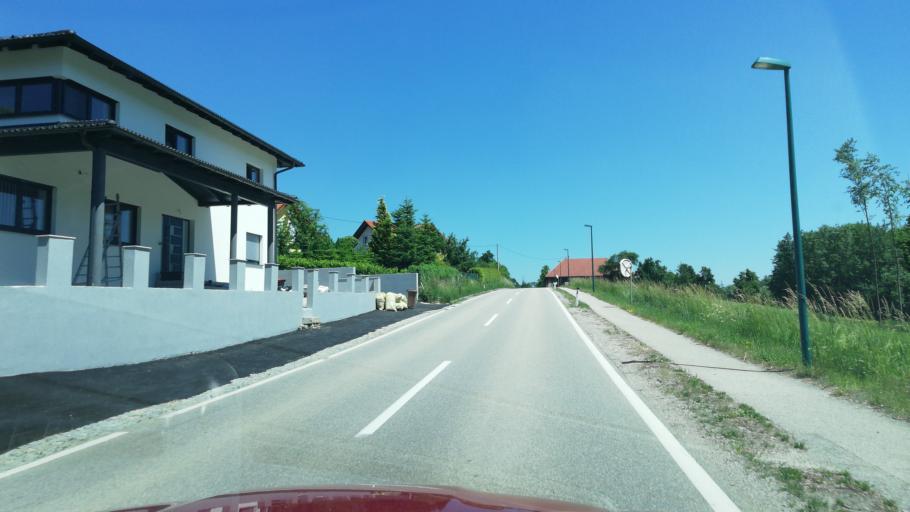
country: AT
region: Upper Austria
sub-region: Wels-Land
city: Pennewang
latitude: 48.1544
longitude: 13.8685
